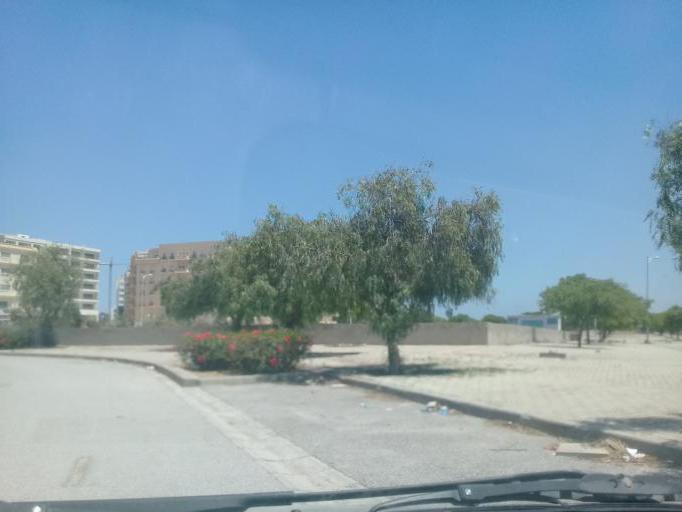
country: TN
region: Tunis
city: La Goulette
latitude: 36.8424
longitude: 10.2799
